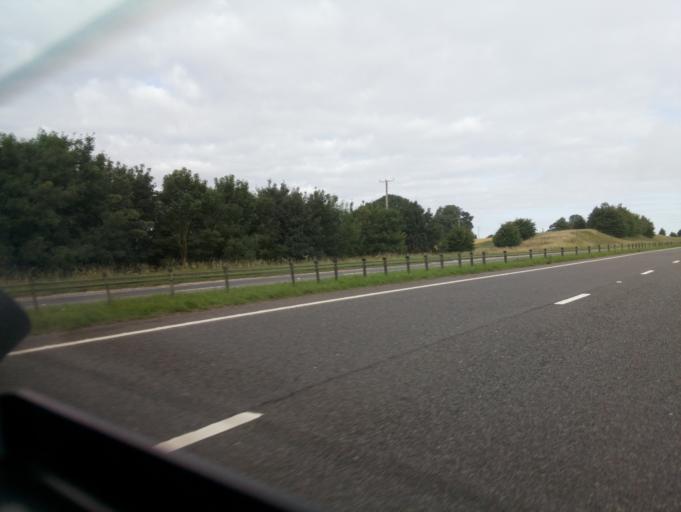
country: GB
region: England
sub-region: Gloucestershire
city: Shurdington
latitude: 51.8112
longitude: -2.0653
